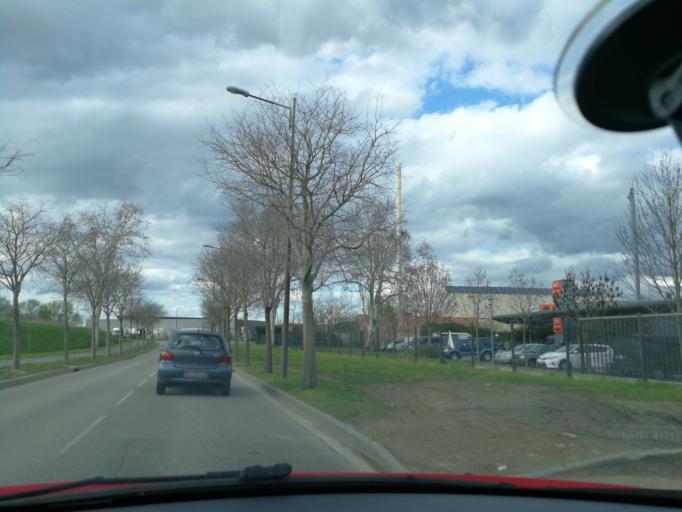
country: FR
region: Midi-Pyrenees
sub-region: Departement de la Haute-Garonne
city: Blagnac
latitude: 43.6279
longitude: 1.4106
